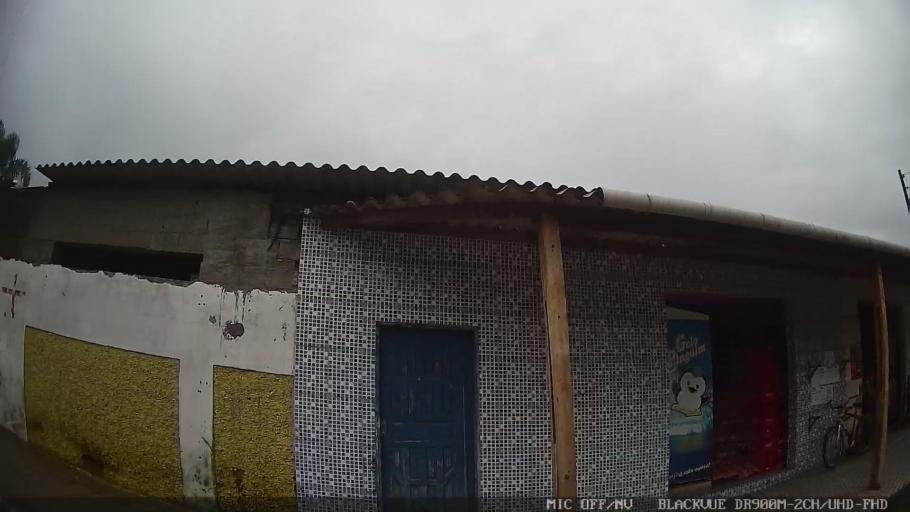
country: BR
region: Sao Paulo
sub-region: Itanhaem
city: Itanhaem
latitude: -24.1774
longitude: -46.8165
